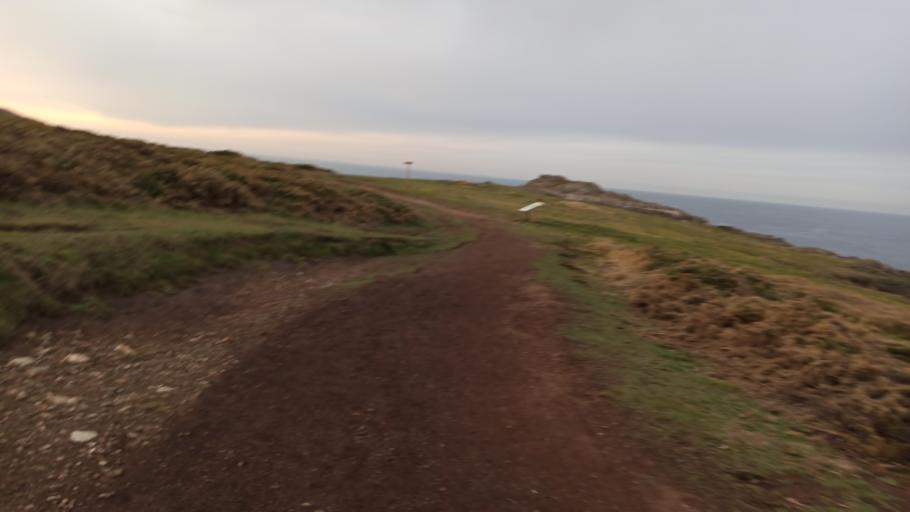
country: ES
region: Galicia
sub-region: Provincia da Coruna
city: A Coruna
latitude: 43.3962
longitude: -8.3454
